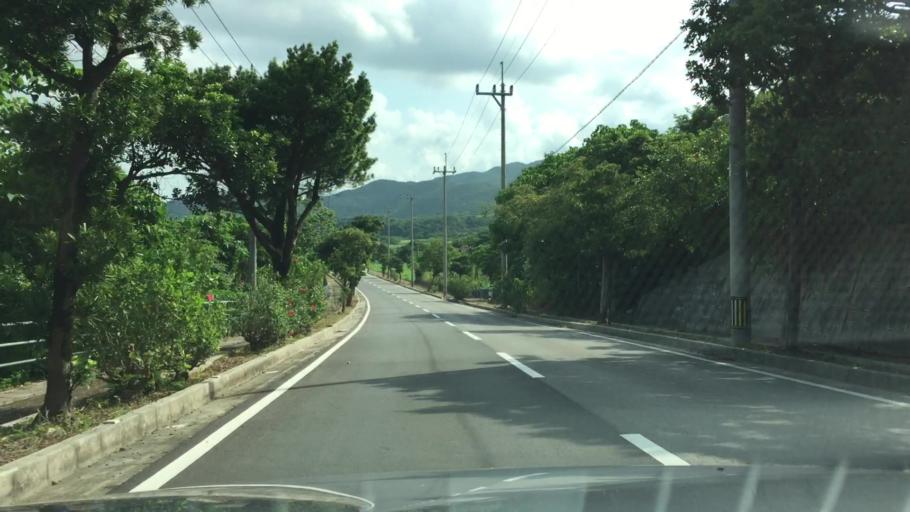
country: JP
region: Okinawa
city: Ishigaki
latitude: 24.4698
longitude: 124.2522
